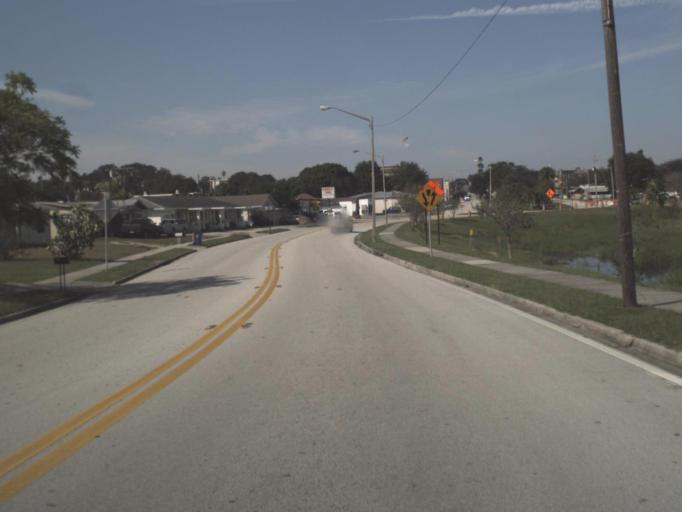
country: US
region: Florida
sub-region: Highlands County
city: Avon Park
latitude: 27.5956
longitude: -81.4962
